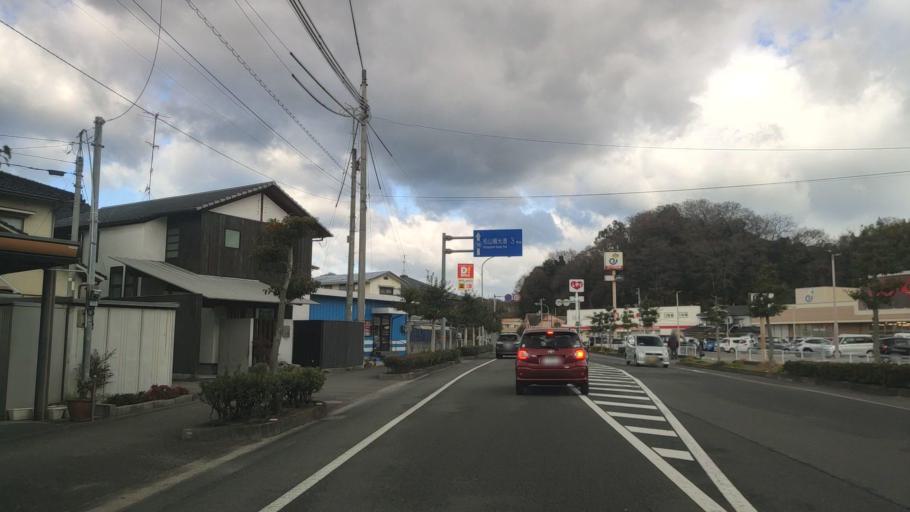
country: JP
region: Ehime
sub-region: Shikoku-chuo Shi
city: Matsuyama
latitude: 33.8670
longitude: 132.7248
